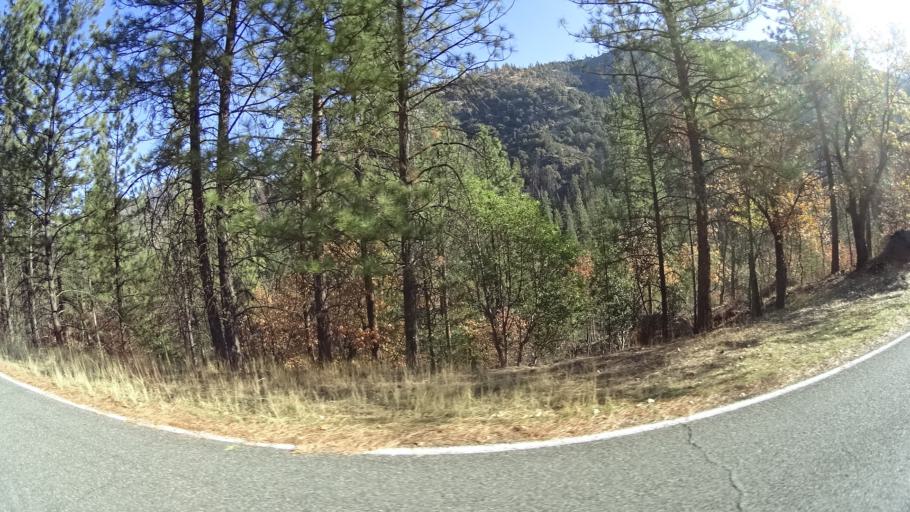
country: US
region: California
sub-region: Siskiyou County
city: Yreka
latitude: 41.8832
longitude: -122.8225
